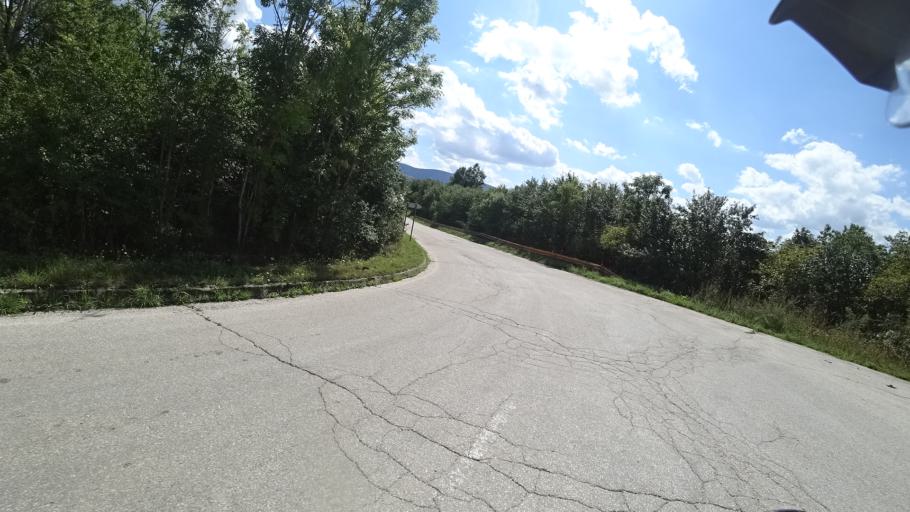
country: BA
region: Federation of Bosnia and Herzegovina
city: Orasac
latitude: 44.4666
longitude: 15.9728
